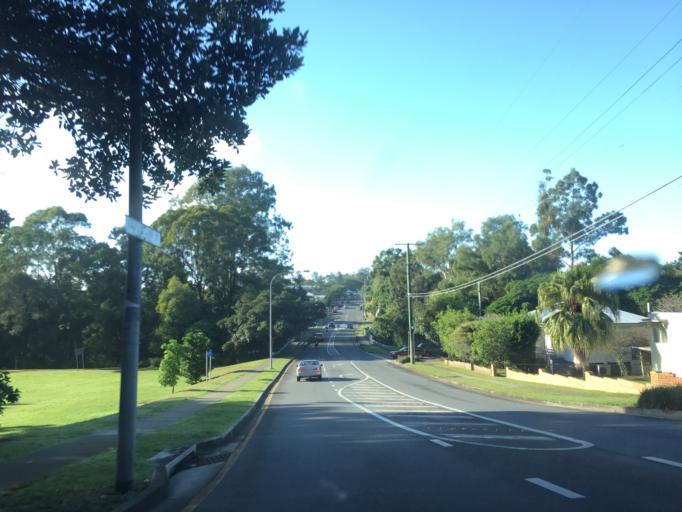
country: AU
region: Queensland
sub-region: Brisbane
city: Milton
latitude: -27.4512
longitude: 152.9784
